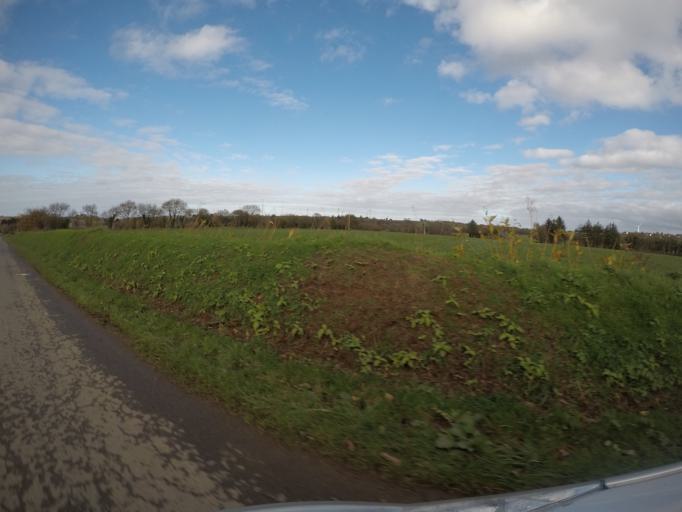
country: FR
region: Brittany
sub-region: Departement des Cotes-d'Armor
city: Louargat
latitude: 48.4669
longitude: -3.3083
